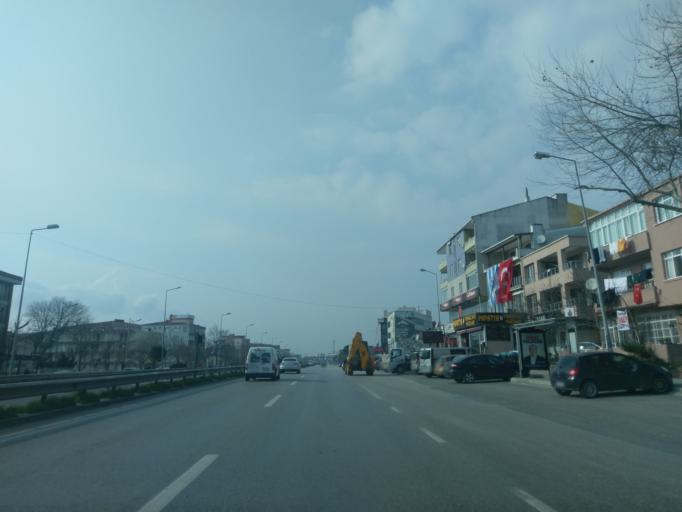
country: TR
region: Istanbul
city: Kumburgaz
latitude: 41.0318
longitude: 28.4532
